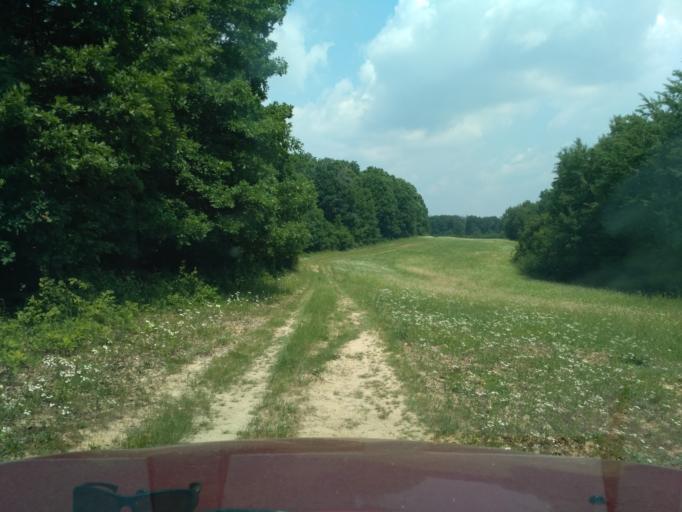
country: SK
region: Kosicky
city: Moldava nad Bodvou
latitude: 48.6285
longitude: 21.0425
